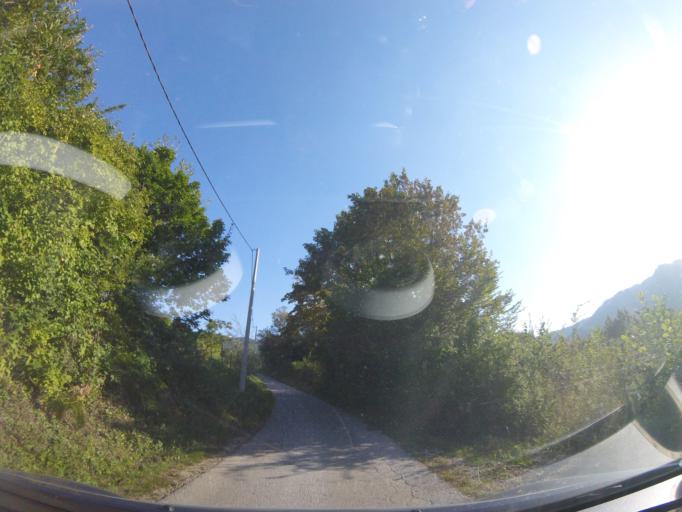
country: HR
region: Zagrebacka
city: Rude
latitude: 45.7574
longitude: 15.6639
